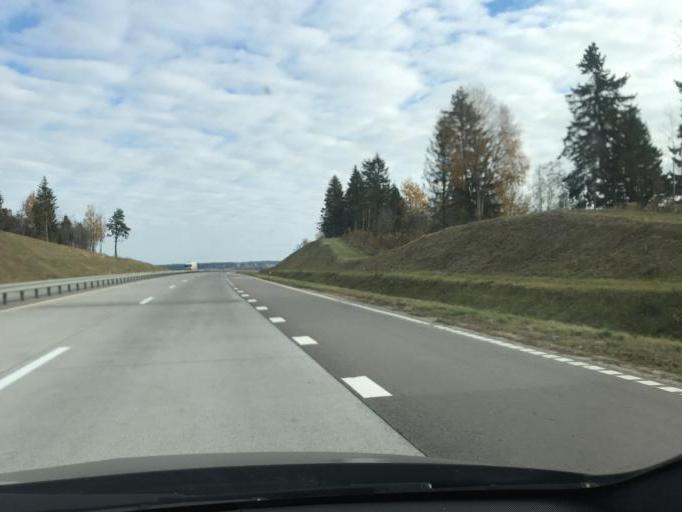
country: BY
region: Minsk
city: Pyatryshki
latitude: 54.0518
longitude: 27.1904
